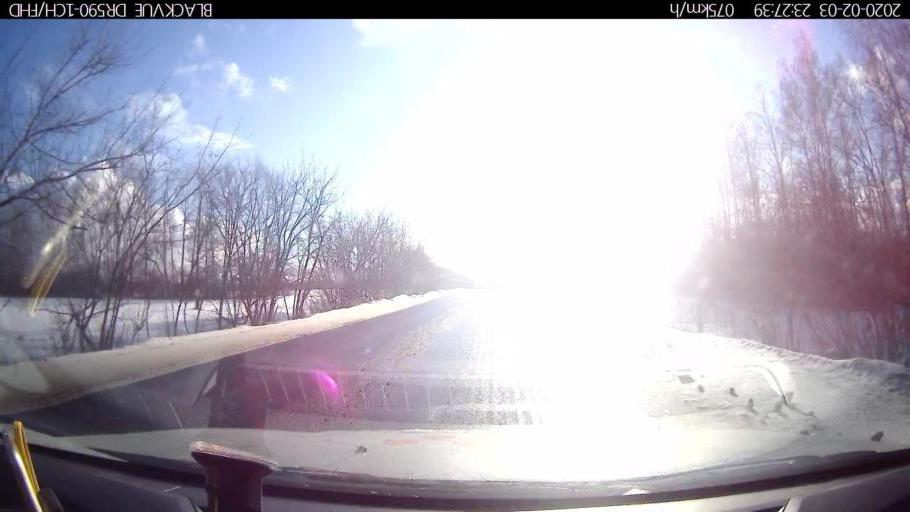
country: RU
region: Nizjnij Novgorod
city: Kstovo
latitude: 55.9810
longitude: 44.2119
